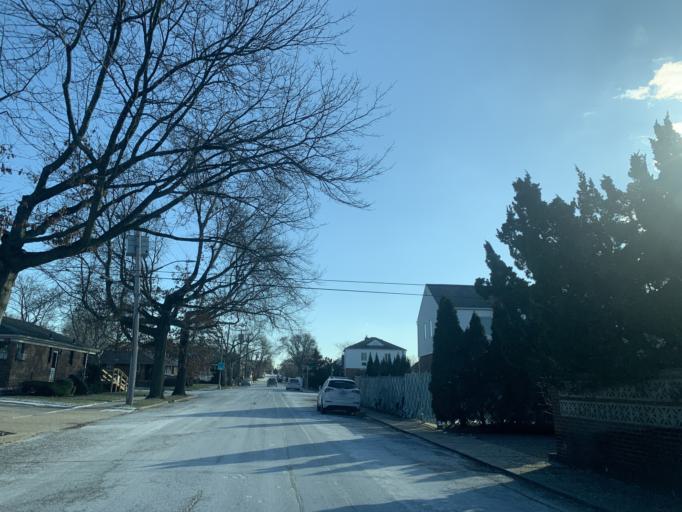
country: US
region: New York
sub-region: Bronx
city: The Bronx
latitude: 40.7941
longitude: -73.8217
